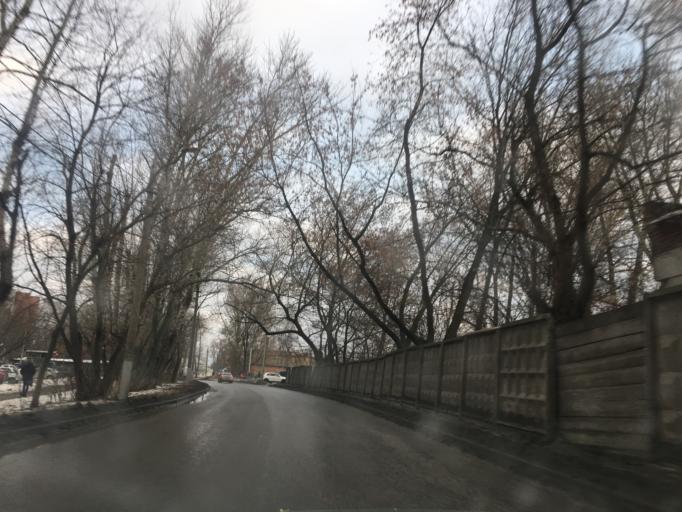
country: RU
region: Tula
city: Tula
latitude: 54.2081
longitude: 37.6254
